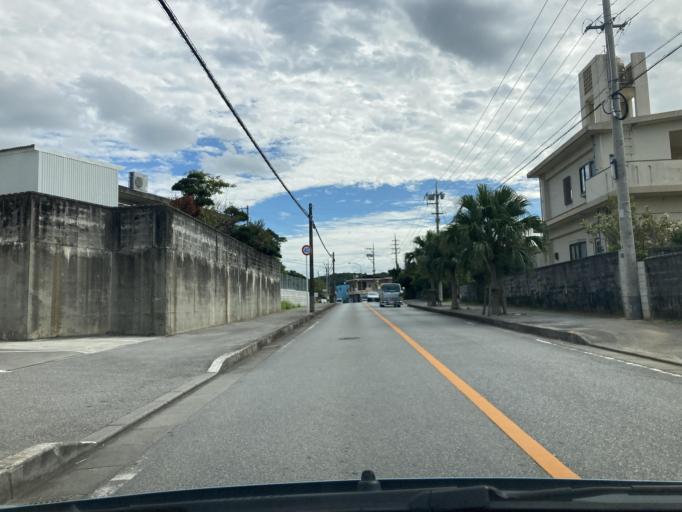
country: JP
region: Okinawa
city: Ishikawa
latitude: 26.4384
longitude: 127.7742
